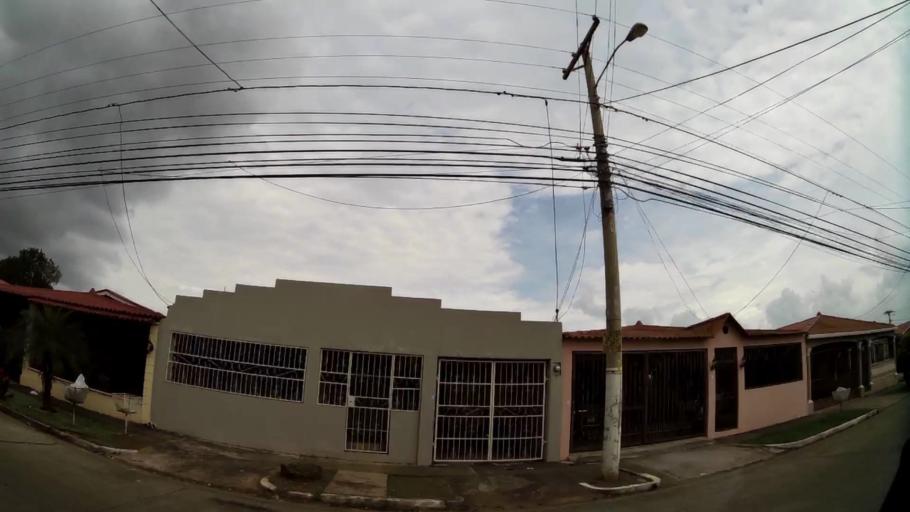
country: PA
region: Panama
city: Tocumen
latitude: 9.0470
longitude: -79.4064
